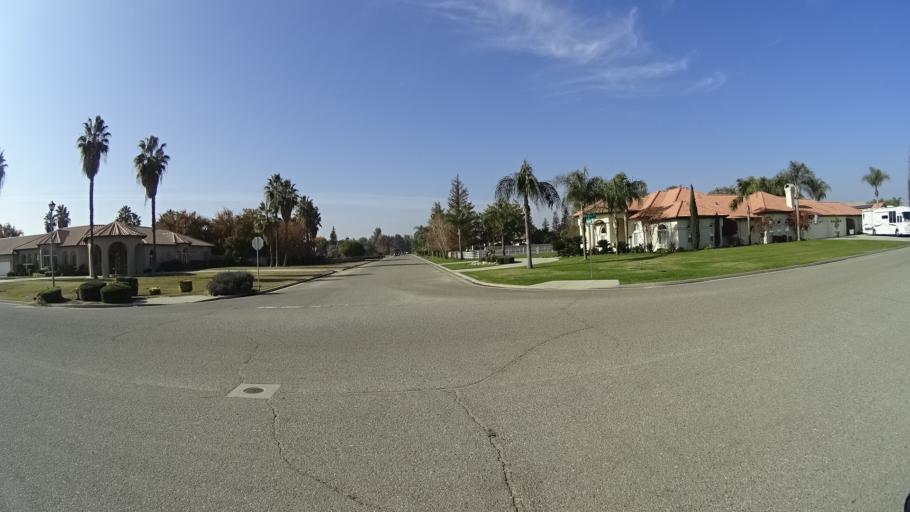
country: US
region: California
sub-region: Kern County
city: Rosedale
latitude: 35.3572
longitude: -119.1898
